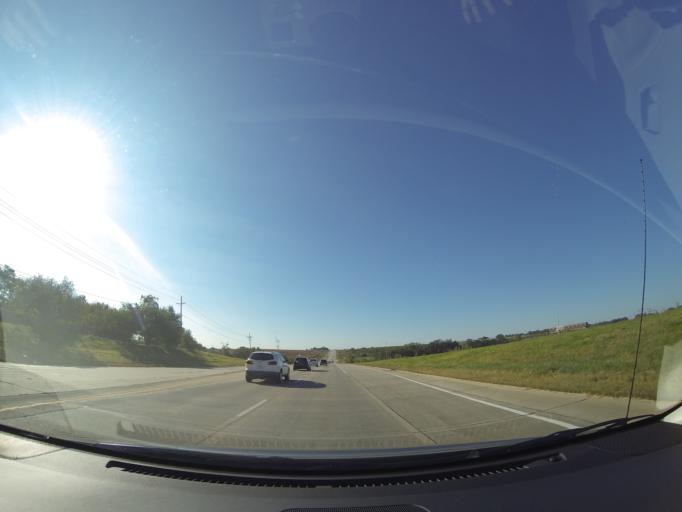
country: US
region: Nebraska
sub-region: Sarpy County
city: Gretna
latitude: 41.2025
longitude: -96.2343
